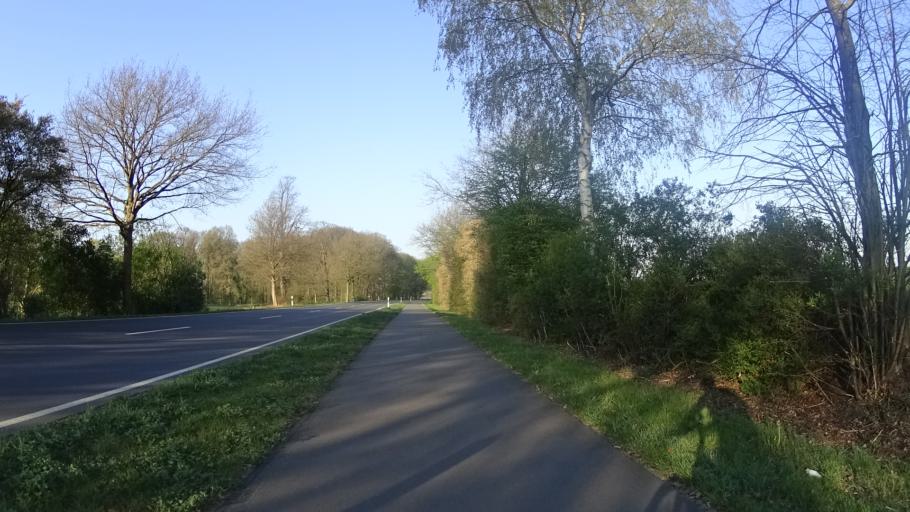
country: DE
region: North Rhine-Westphalia
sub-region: Regierungsbezirk Dusseldorf
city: Hunxe
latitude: 51.6663
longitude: 6.8239
